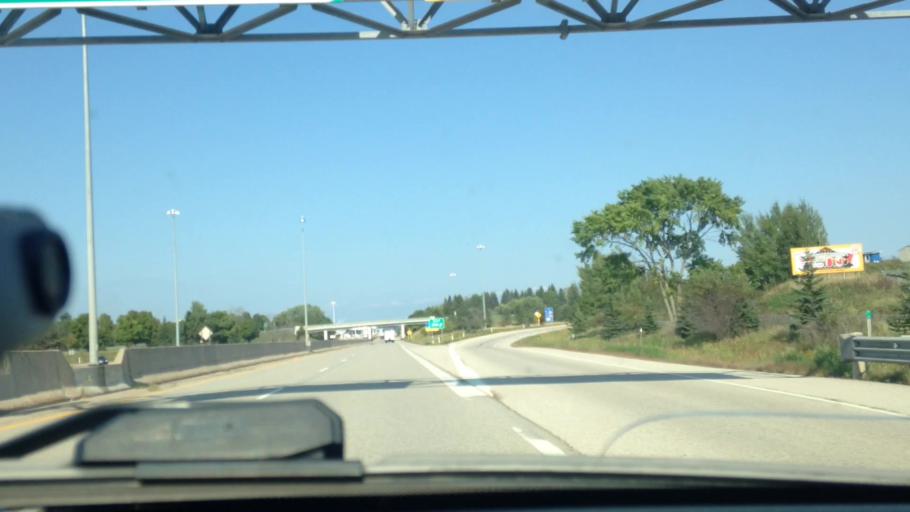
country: US
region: Michigan
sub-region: Chippewa County
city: Sault Ste. Marie
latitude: 46.4889
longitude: -84.3742
